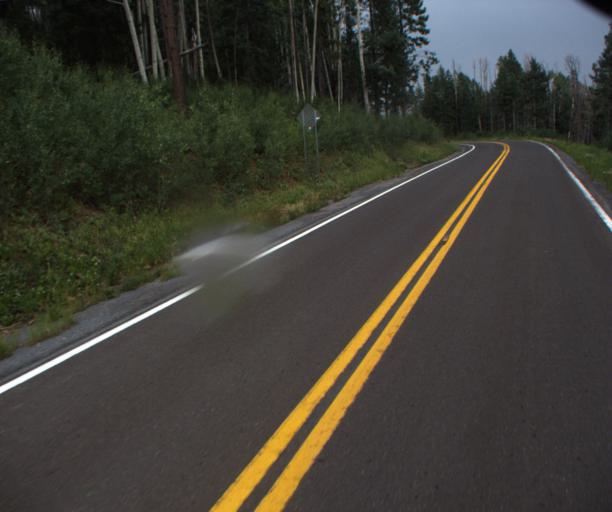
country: US
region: Arizona
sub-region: Greenlee County
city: Morenci
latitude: 33.5709
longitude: -109.3581
